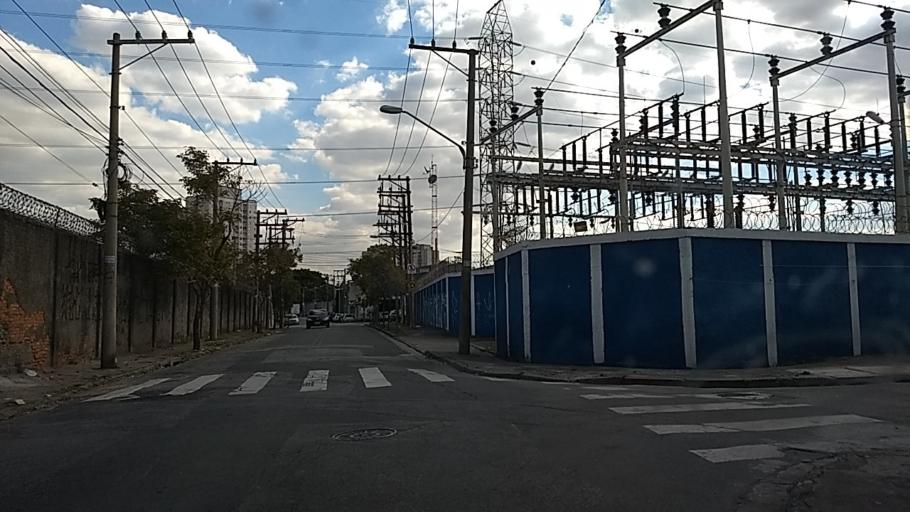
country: BR
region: Sao Paulo
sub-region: Sao Paulo
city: Sao Paulo
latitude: -23.5179
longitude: -46.5980
